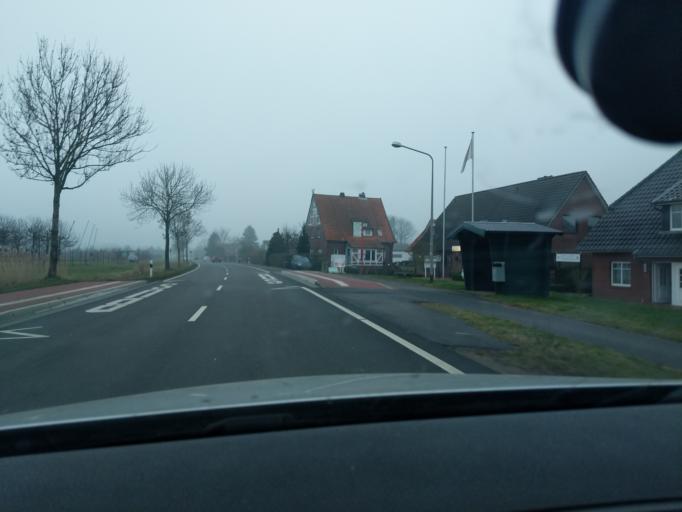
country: DE
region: Lower Saxony
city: Jork
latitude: 53.5431
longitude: 9.6804
